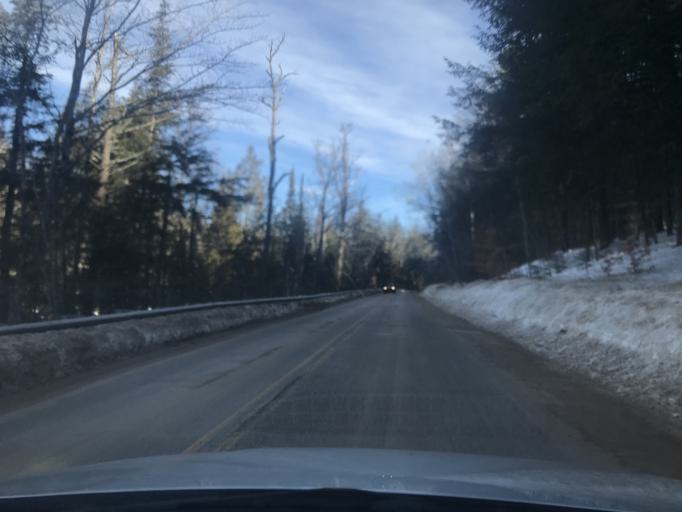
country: US
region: Michigan
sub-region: Dickinson County
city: Kingsford
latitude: 45.4089
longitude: -88.3657
